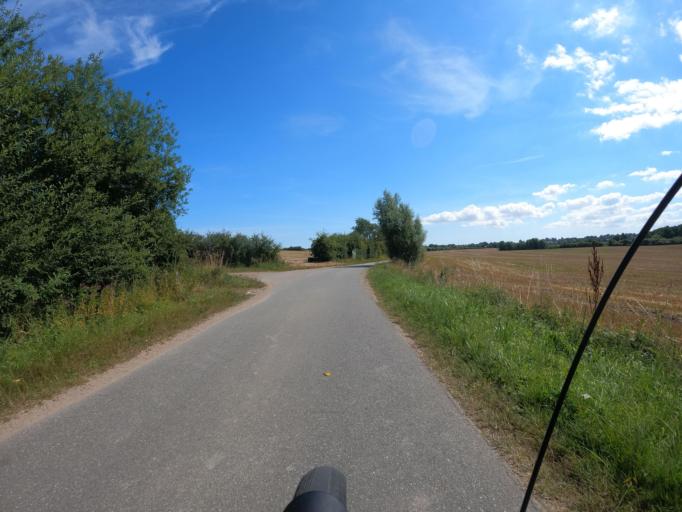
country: DE
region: Schleswig-Holstein
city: Dollerup
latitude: 54.7806
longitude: 9.7134
